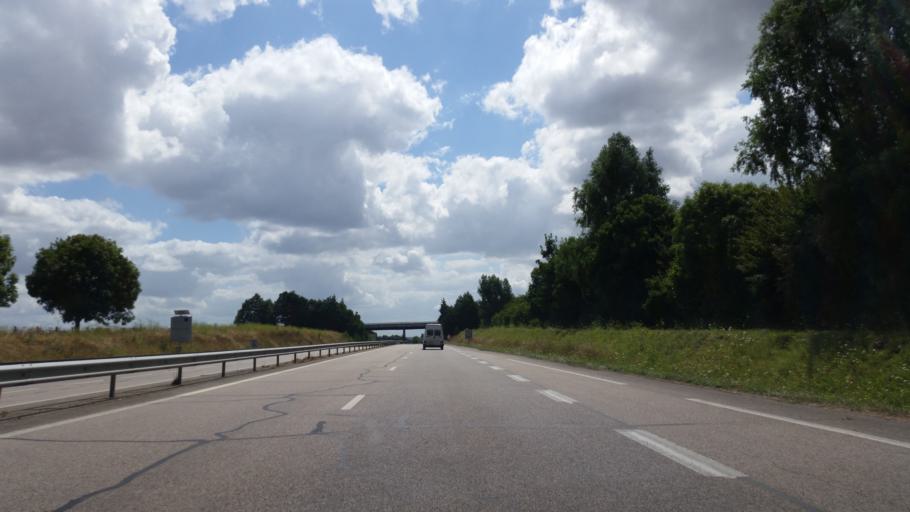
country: FR
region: Lower Normandy
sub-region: Departement du Calvados
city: Falaise
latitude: 48.9323
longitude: -0.2081
